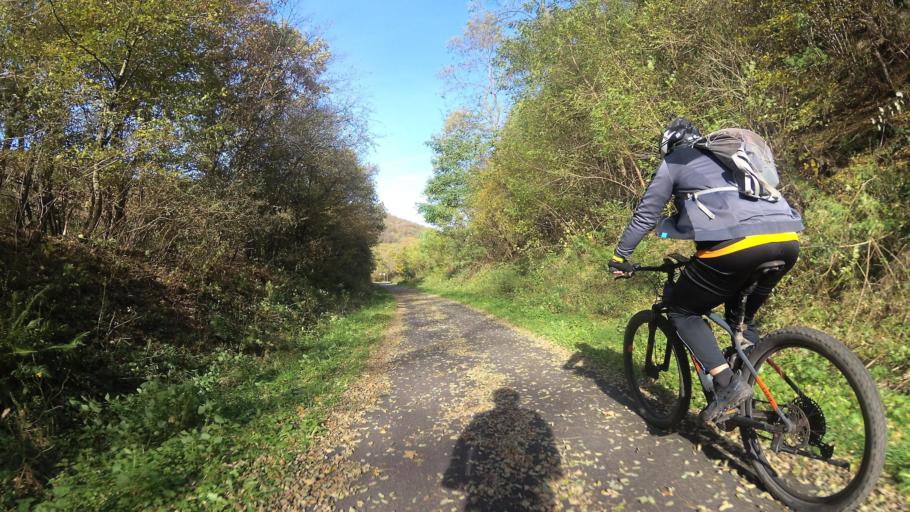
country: DE
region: Rheinland-Pfalz
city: Morscheid
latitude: 49.7310
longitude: 6.7420
